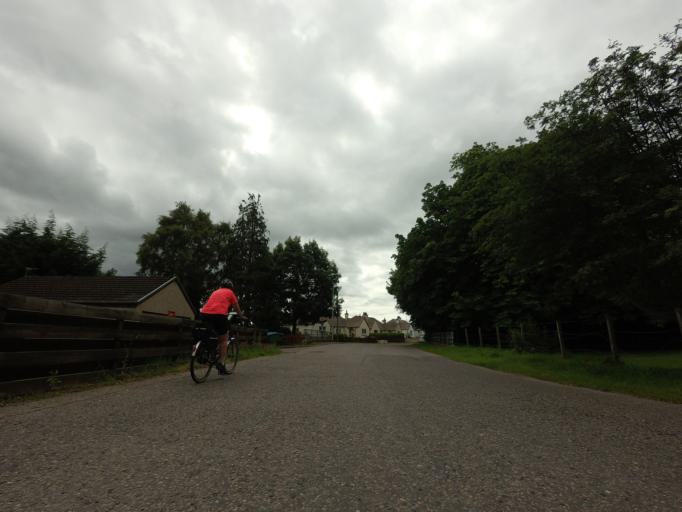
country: GB
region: Scotland
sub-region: Moray
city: Forres
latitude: 57.6033
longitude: -3.6925
